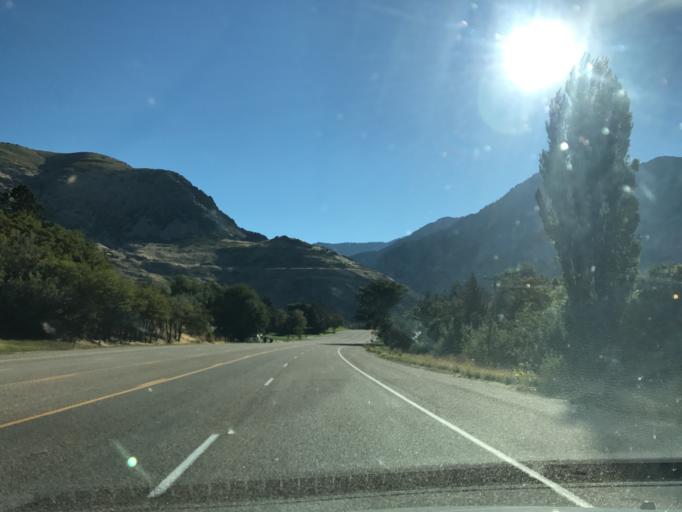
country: US
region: Utah
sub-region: Weber County
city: Ogden
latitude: 41.2401
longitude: -111.9396
